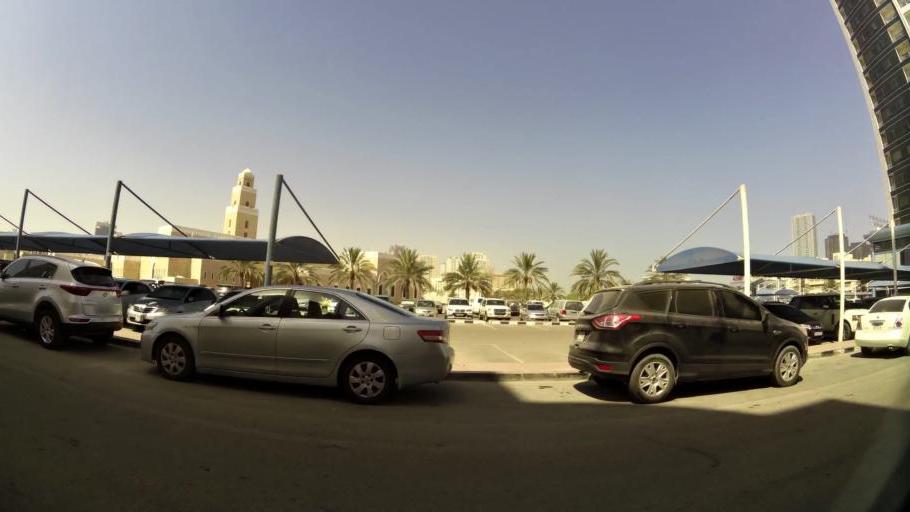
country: AE
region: Ajman
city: Ajman
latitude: 25.4028
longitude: 55.4401
